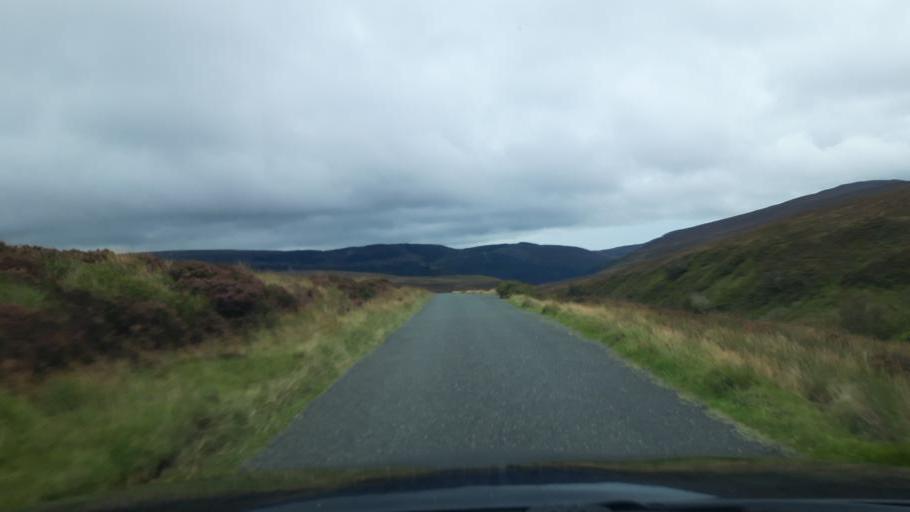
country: IE
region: Leinster
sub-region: Wicklow
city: Enniskerry
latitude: 53.1314
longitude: -6.2979
